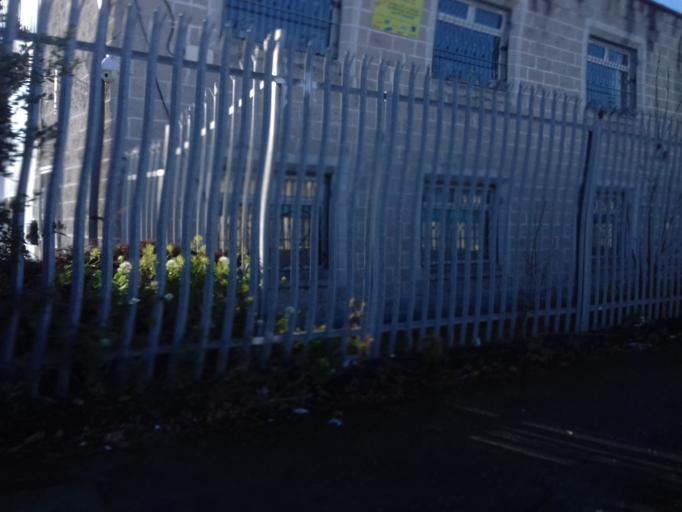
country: IE
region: Leinster
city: Cabra
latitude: 53.3728
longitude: -6.2945
